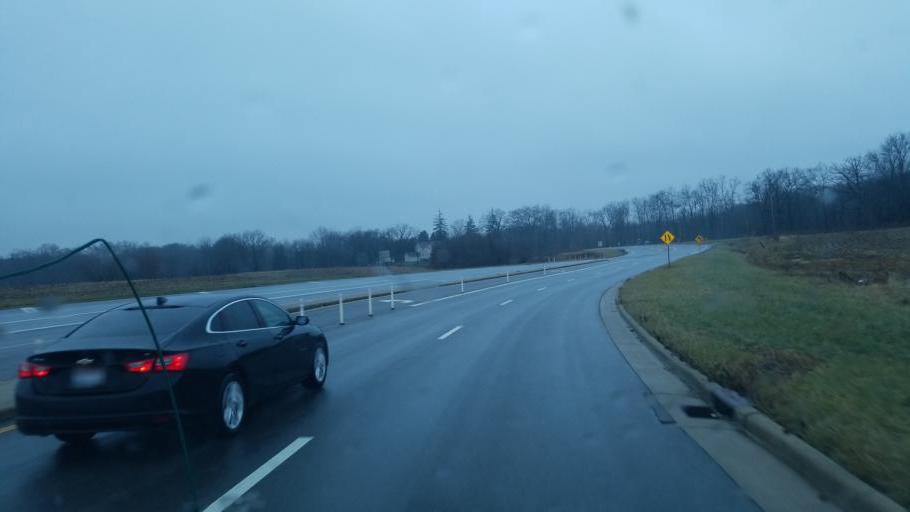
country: US
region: Ohio
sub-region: Delaware County
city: Lewis Center
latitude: 40.1948
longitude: -83.0289
